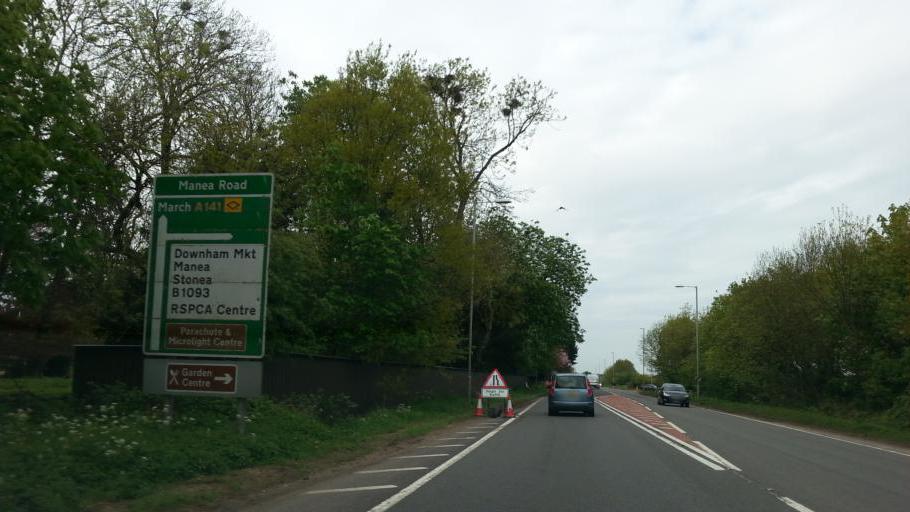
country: GB
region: England
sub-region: Cambridgeshire
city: Doddington
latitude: 52.5067
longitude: 0.0850
